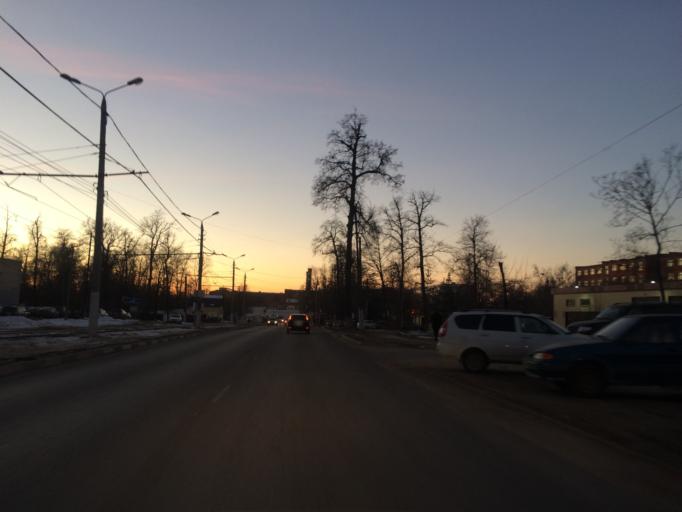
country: RU
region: Tula
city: Tula
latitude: 54.2205
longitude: 37.6918
